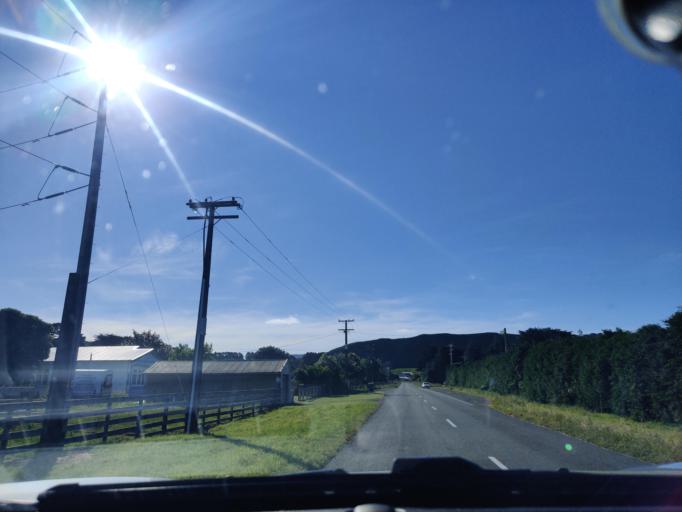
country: NZ
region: Manawatu-Wanganui
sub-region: Palmerston North City
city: Palmerston North
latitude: -40.5167
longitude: 175.7521
